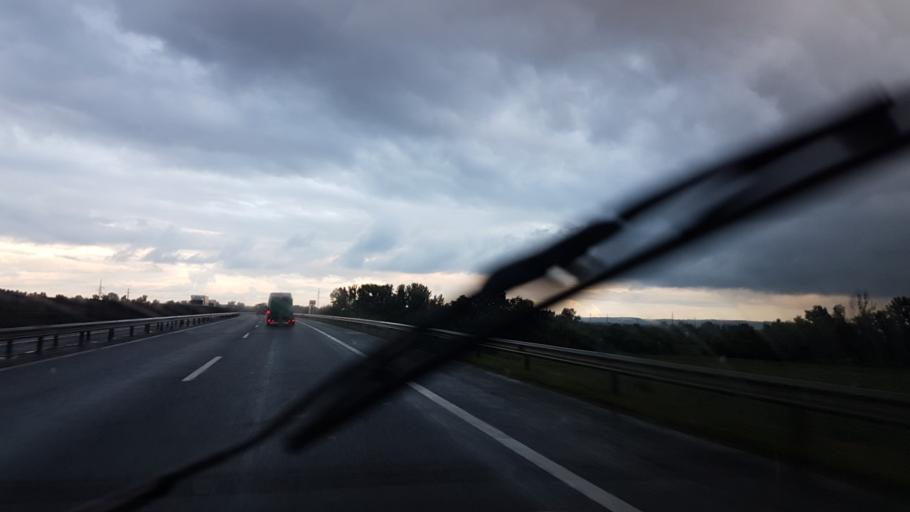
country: HU
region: Borsod-Abauj-Zemplen
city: Felsozsolca
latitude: 48.0995
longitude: 20.8464
